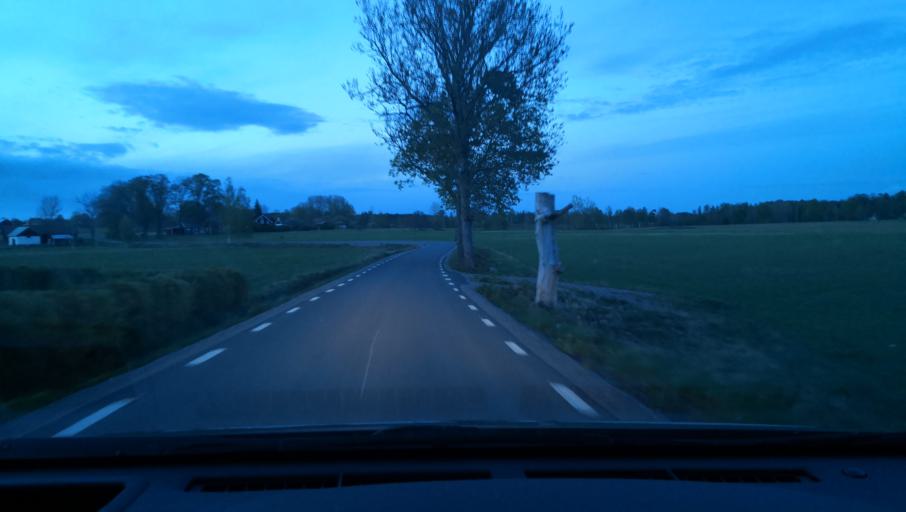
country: SE
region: OErebro
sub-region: Askersunds Kommun
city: Asbro
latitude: 59.0627
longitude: 14.9488
